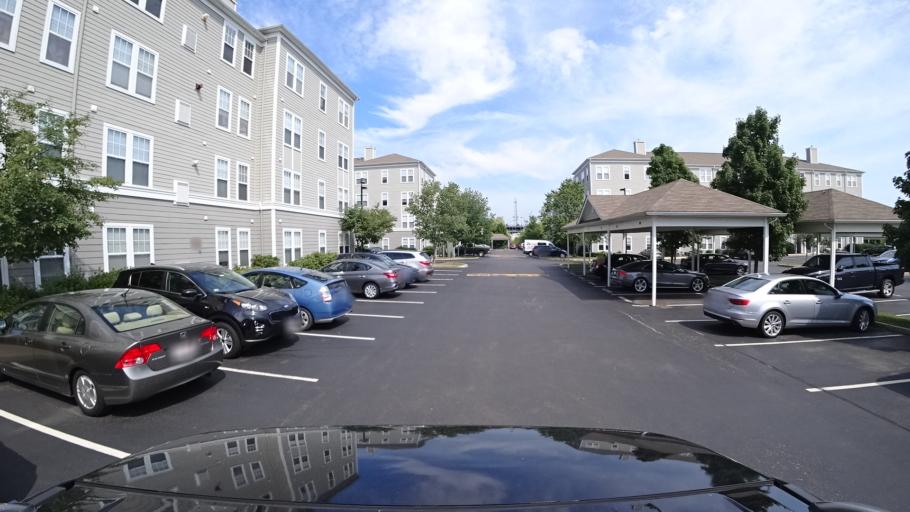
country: US
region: Massachusetts
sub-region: Norfolk County
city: Dedham
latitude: 42.2282
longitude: -71.1741
